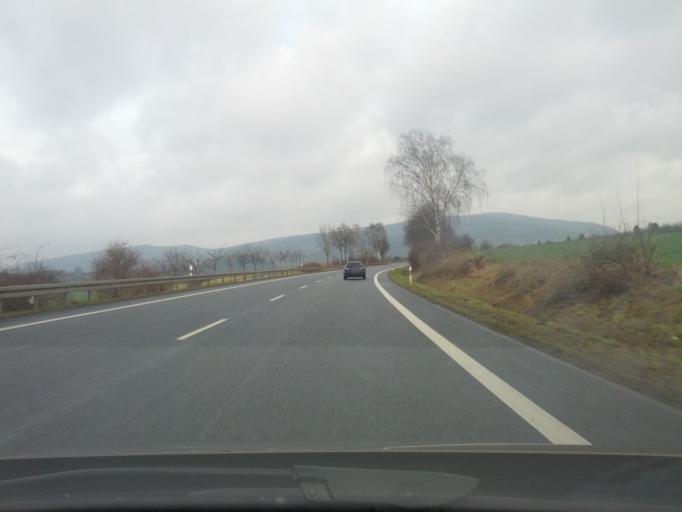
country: DE
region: Hesse
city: Witzenhausen
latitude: 51.3244
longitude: 9.8864
